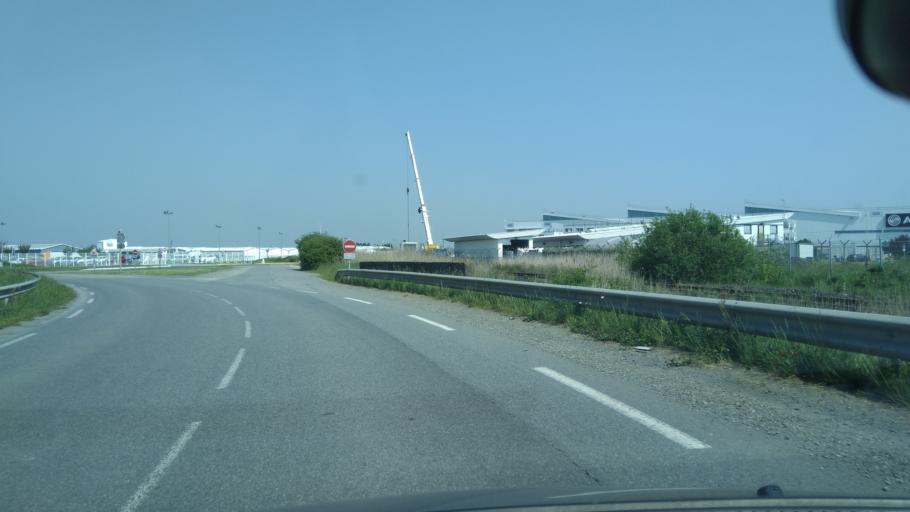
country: FR
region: Pays de la Loire
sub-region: Departement de la Loire-Atlantique
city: Trignac
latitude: 47.3090
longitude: -2.1727
